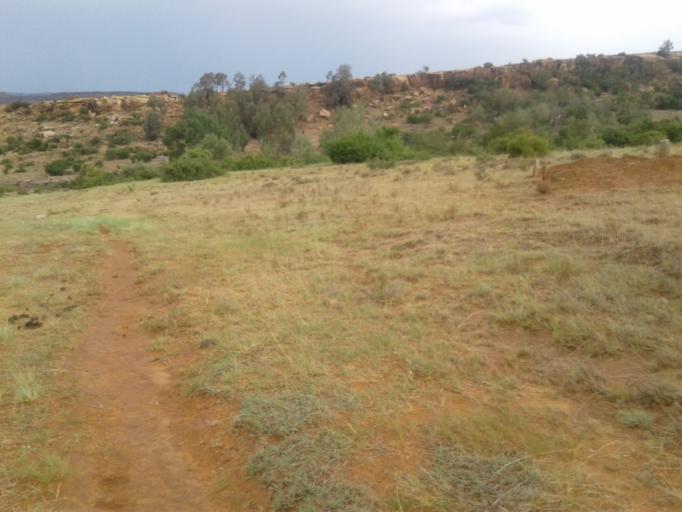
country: LS
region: Quthing
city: Quthing
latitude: -30.3841
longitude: 27.5638
